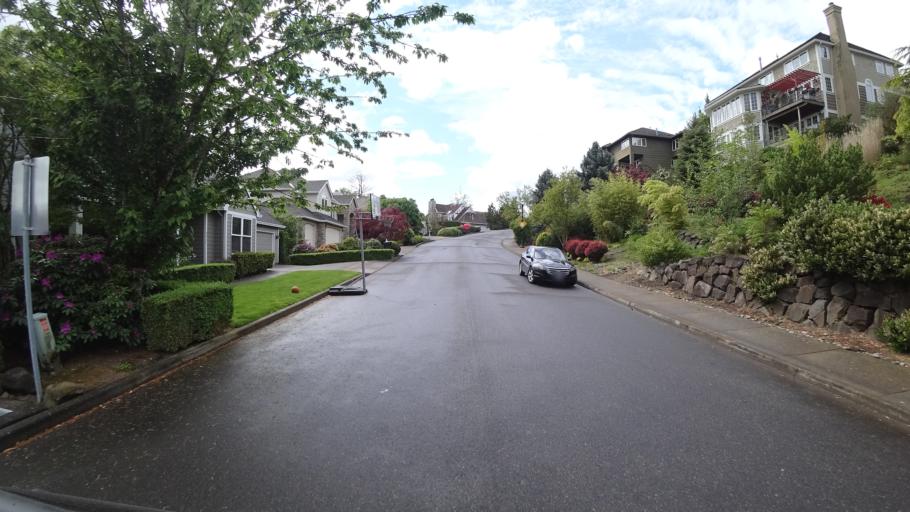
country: US
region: Oregon
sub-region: Washington County
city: West Haven
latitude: 45.5391
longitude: -122.7713
